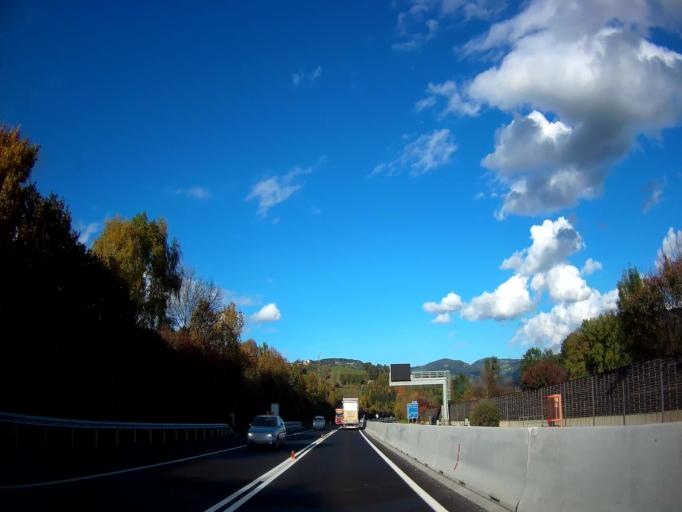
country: AT
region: Carinthia
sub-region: Politischer Bezirk Wolfsberg
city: Wolfsberg
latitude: 46.8395
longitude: 14.8228
